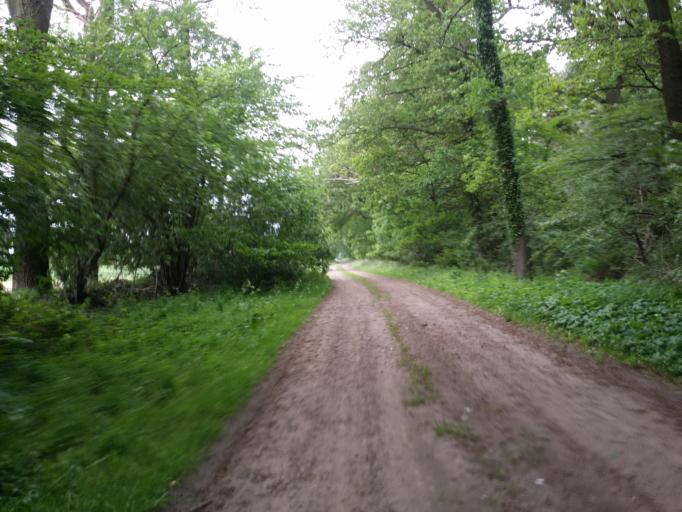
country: DE
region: Lower Saxony
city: Hude
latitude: 53.0529
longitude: 8.4490
